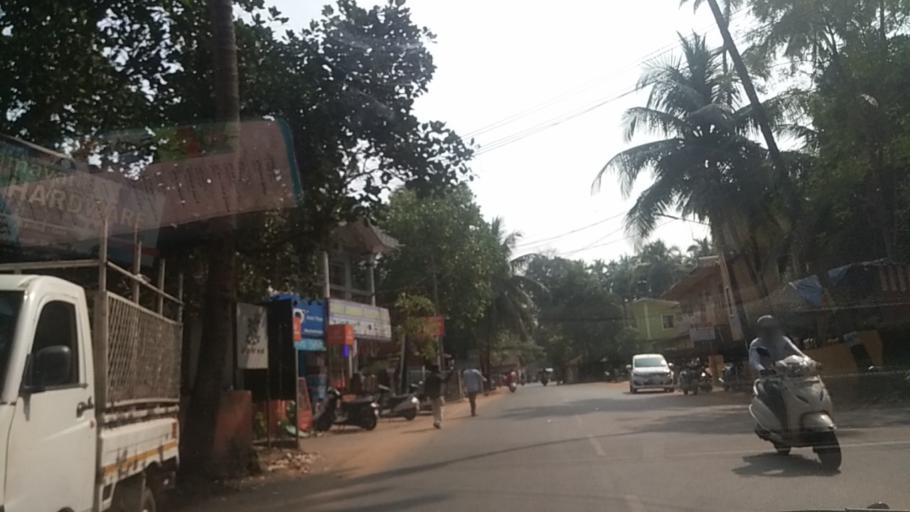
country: IN
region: Goa
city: Calangute
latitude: 15.5516
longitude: 73.7642
